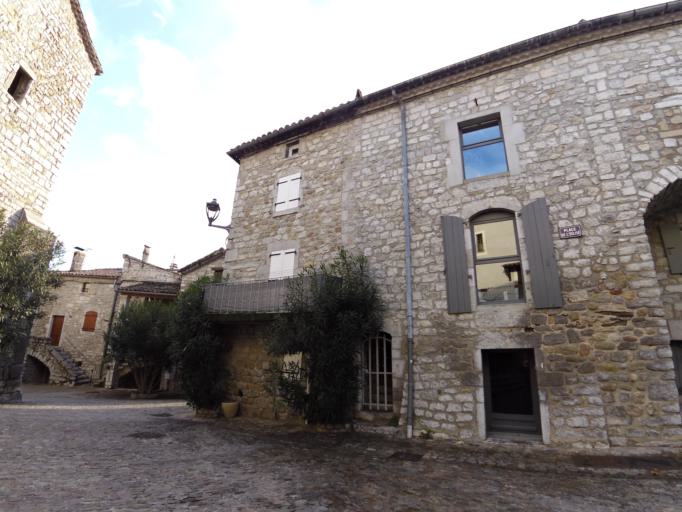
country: FR
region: Rhone-Alpes
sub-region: Departement de l'Ardeche
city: Ruoms
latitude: 44.4537
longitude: 4.3406
